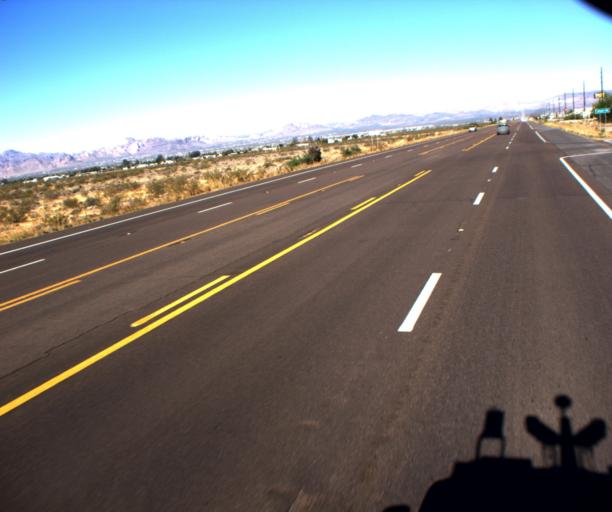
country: US
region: Arizona
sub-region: Mohave County
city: Golden Valley
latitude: 35.2215
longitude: -114.2049
